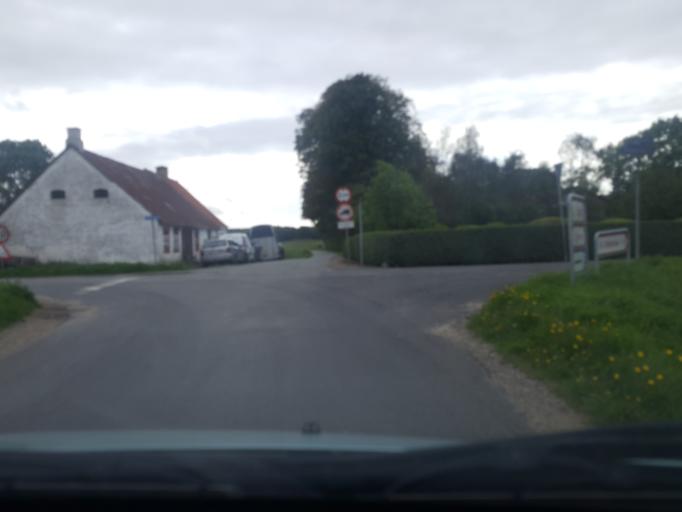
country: DK
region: Zealand
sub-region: Soro Kommune
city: Soro
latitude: 55.4611
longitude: 11.5177
